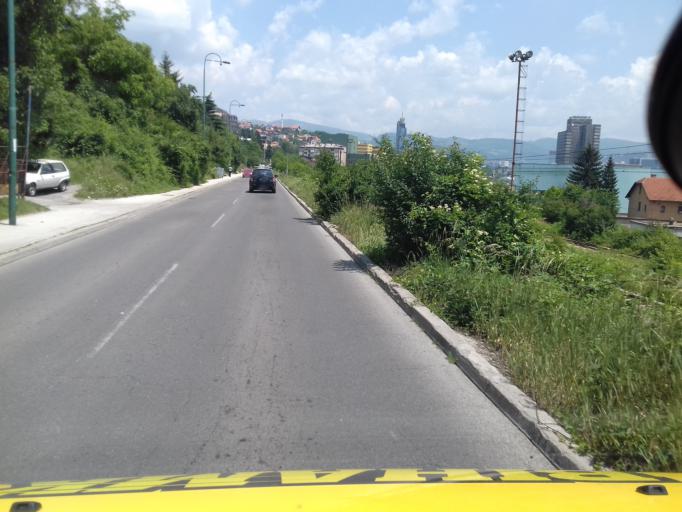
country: BA
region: Federation of Bosnia and Herzegovina
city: Kobilja Glava
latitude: 43.8574
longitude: 18.3811
